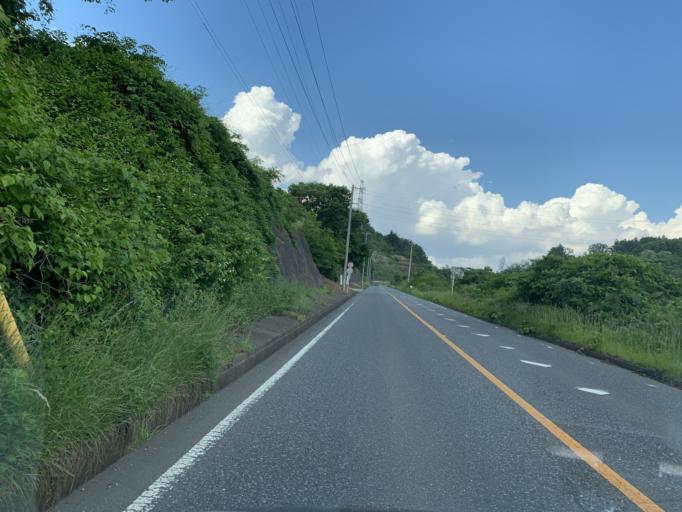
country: JP
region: Miyagi
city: Wakuya
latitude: 38.5650
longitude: 141.1373
